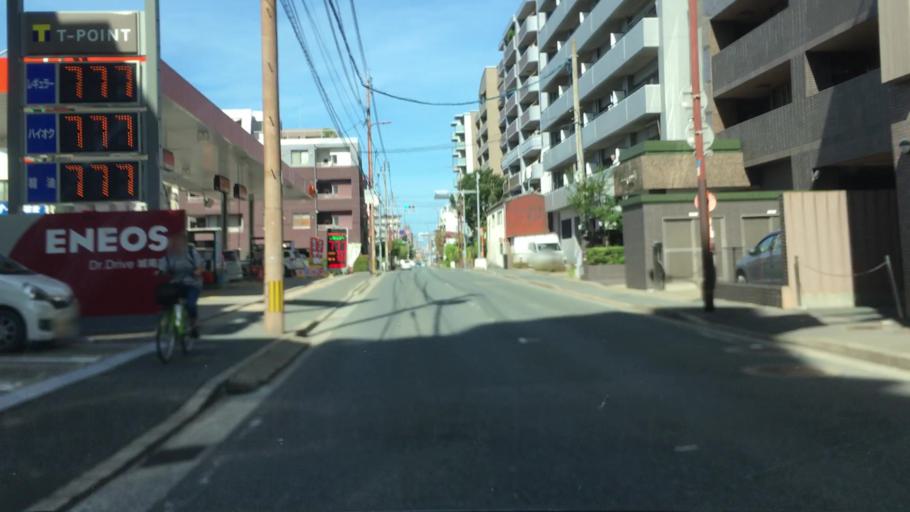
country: JP
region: Fukuoka
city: Fukuoka-shi
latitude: 33.5753
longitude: 130.3674
